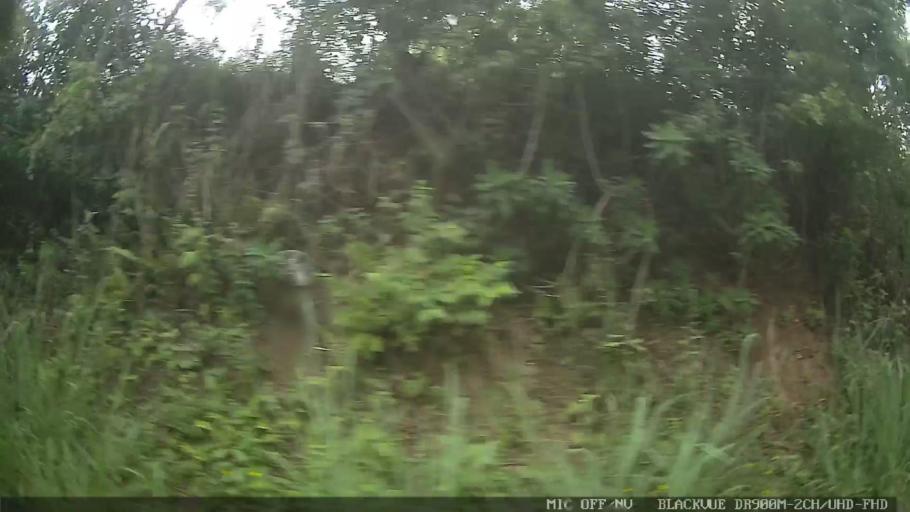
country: BR
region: Sao Paulo
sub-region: Atibaia
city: Atibaia
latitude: -23.1580
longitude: -46.5982
